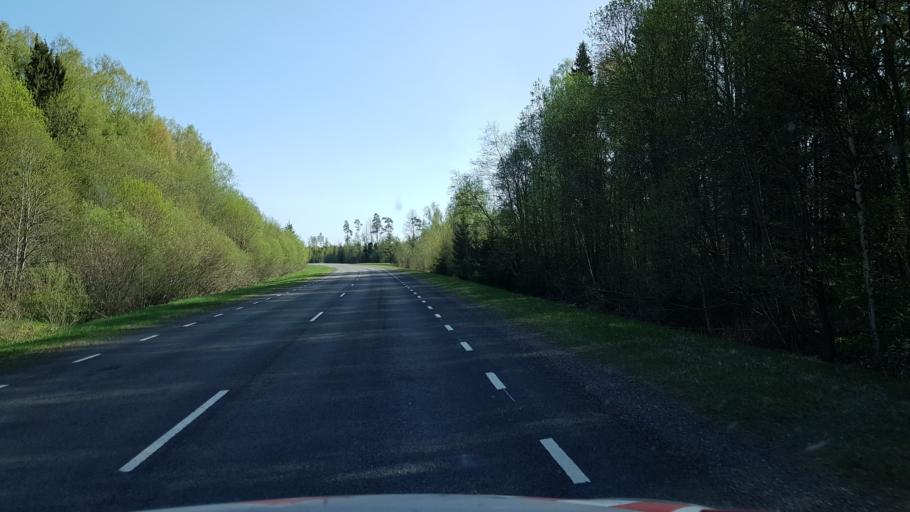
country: EE
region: Viljandimaa
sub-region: Karksi vald
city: Karksi-Nuia
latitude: 58.2182
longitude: 25.5636
